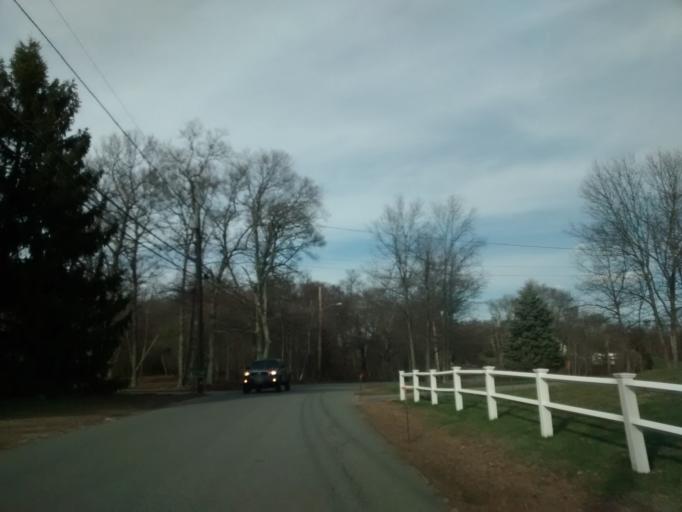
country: US
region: Massachusetts
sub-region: Norfolk County
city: Plainville
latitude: 42.0066
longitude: -71.3664
